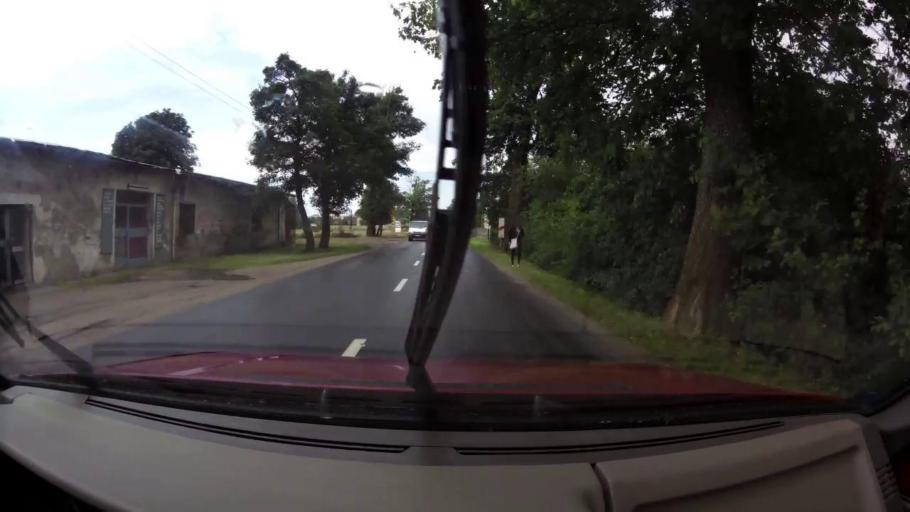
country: PL
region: West Pomeranian Voivodeship
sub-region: Koszalin
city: Koszalin
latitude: 54.1765
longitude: 16.1645
